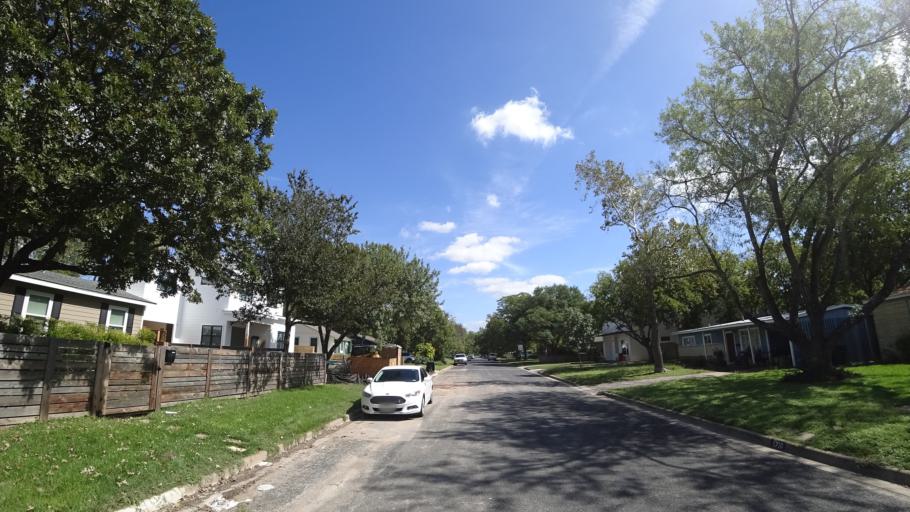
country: US
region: Texas
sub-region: Travis County
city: Austin
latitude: 30.3467
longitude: -97.7284
